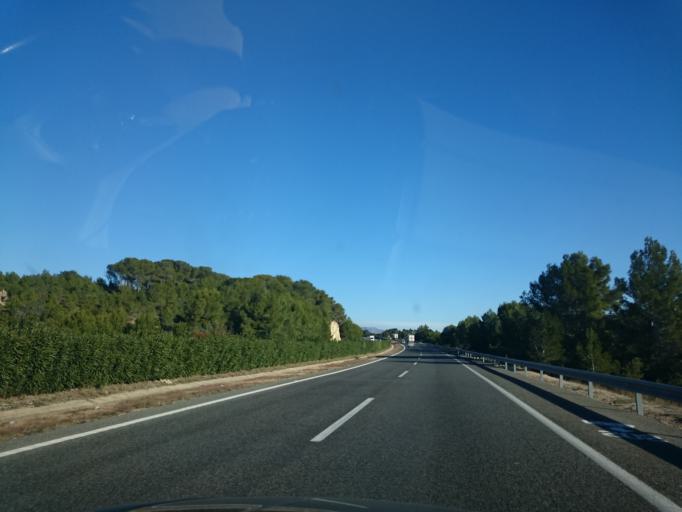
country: ES
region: Catalonia
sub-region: Provincia de Tarragona
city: L'Ampolla
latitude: 40.8331
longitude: 0.7399
